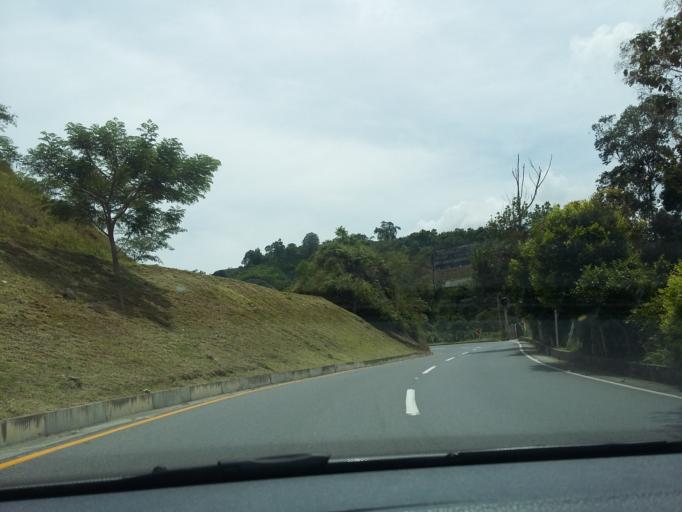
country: CO
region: Santander
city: Bucaramanga
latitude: 7.1148
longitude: -73.0795
